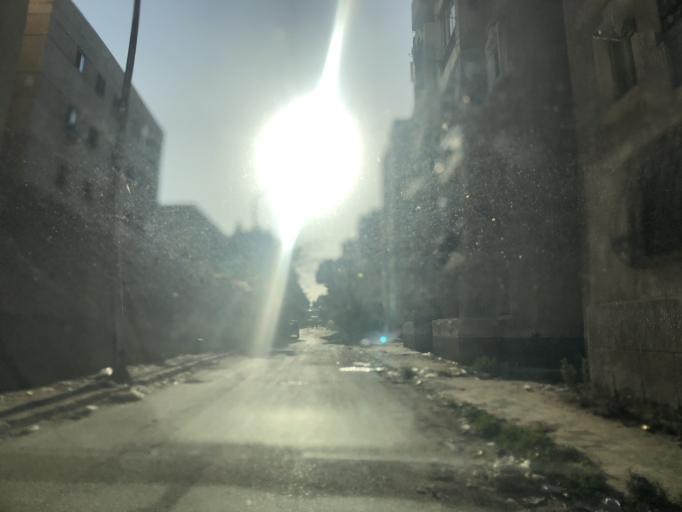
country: EG
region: Al Jizah
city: Al Jizah
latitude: 29.9883
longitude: 31.1017
